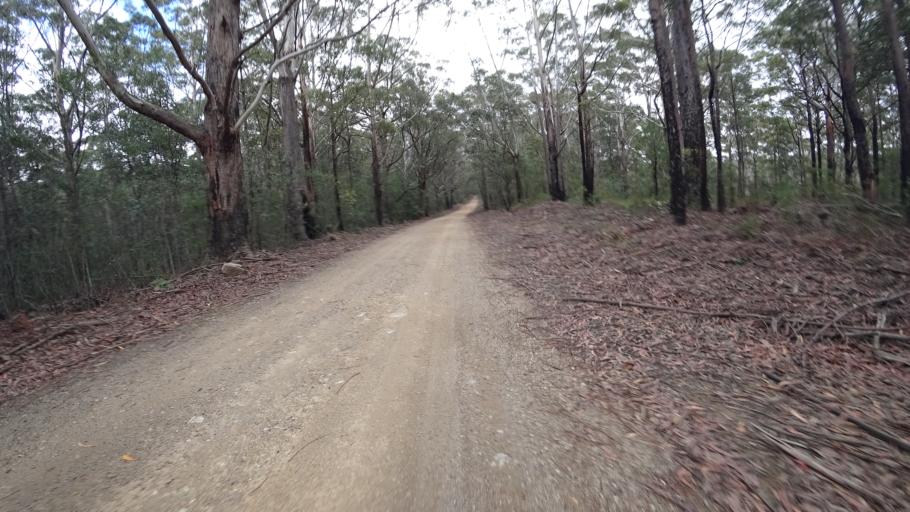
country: AU
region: New South Wales
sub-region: Shoalhaven Shire
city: Milton
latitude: -35.1671
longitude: 150.4125
